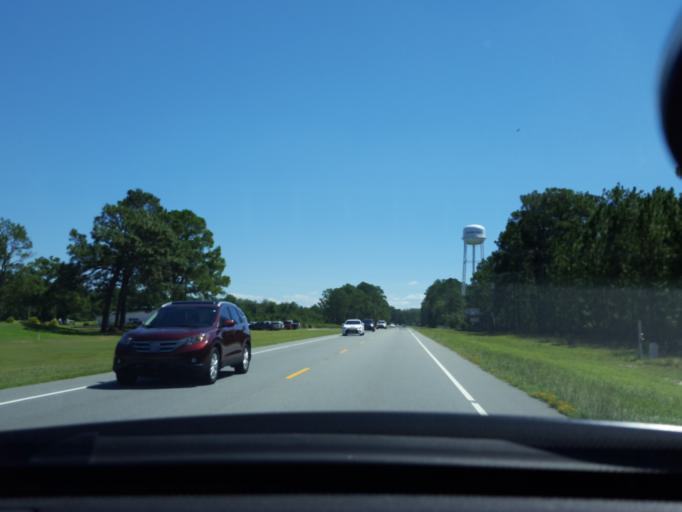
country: US
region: North Carolina
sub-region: Bladen County
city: Elizabethtown
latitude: 34.6496
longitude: -78.5361
